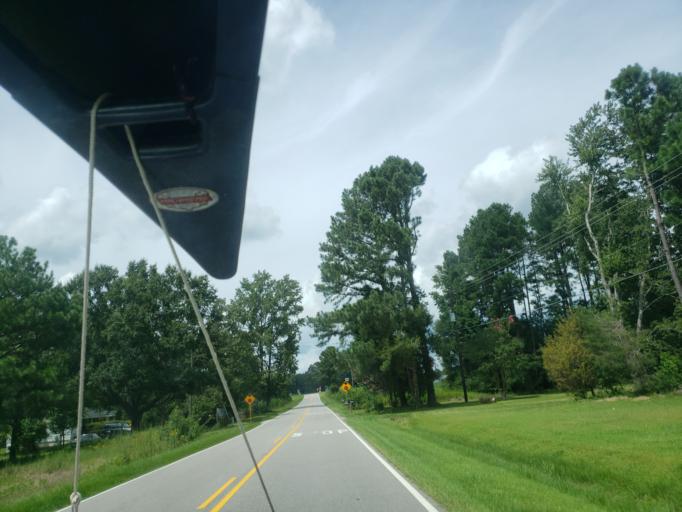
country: US
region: North Carolina
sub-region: Wake County
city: Rolesville
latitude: 35.8903
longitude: -78.4270
